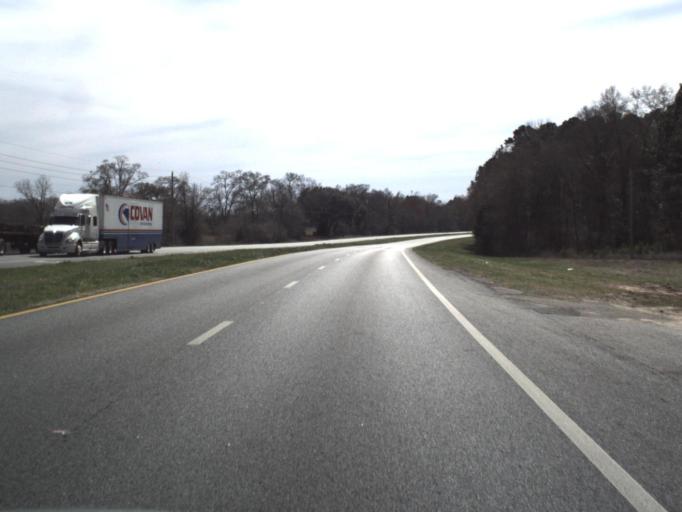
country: US
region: Florida
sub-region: Jackson County
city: Marianna
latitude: 30.7735
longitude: -85.3742
